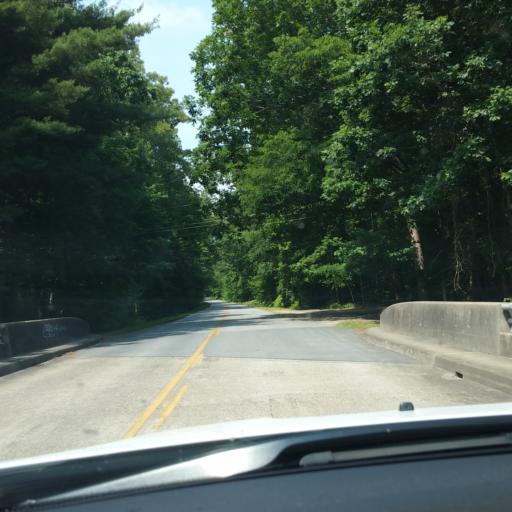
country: US
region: North Carolina
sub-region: Buncombe County
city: Biltmore Forest
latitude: 35.5248
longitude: -82.5187
